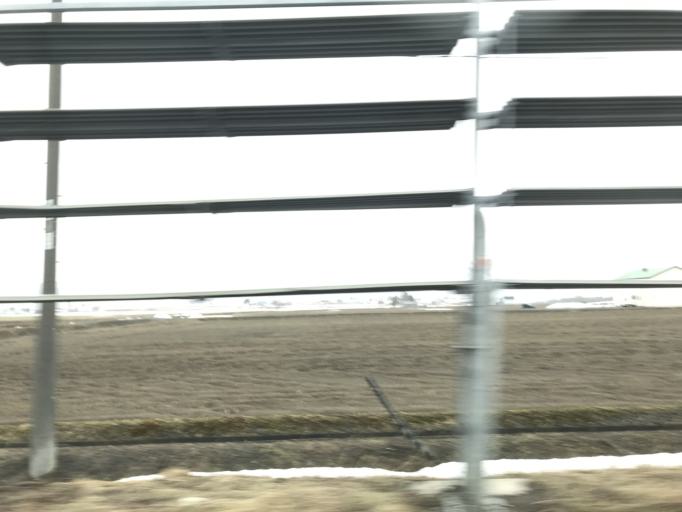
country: JP
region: Hokkaido
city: Nayoro
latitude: 44.2299
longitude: 142.3947
